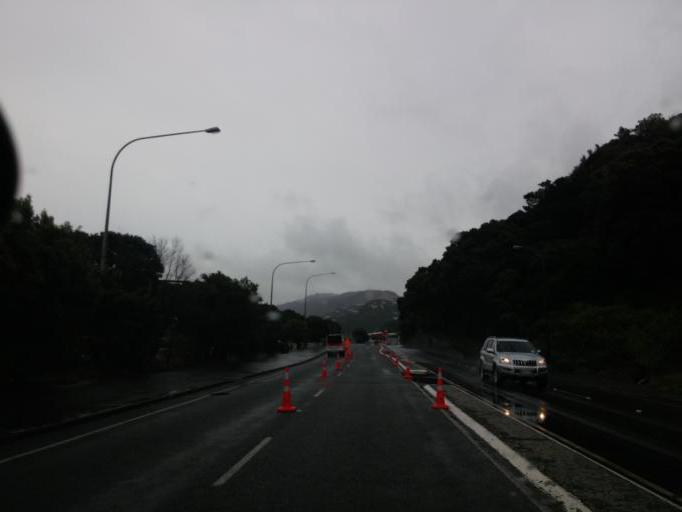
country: NZ
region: Wellington
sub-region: Wellington City
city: Wellington
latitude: -41.2534
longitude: 174.8028
